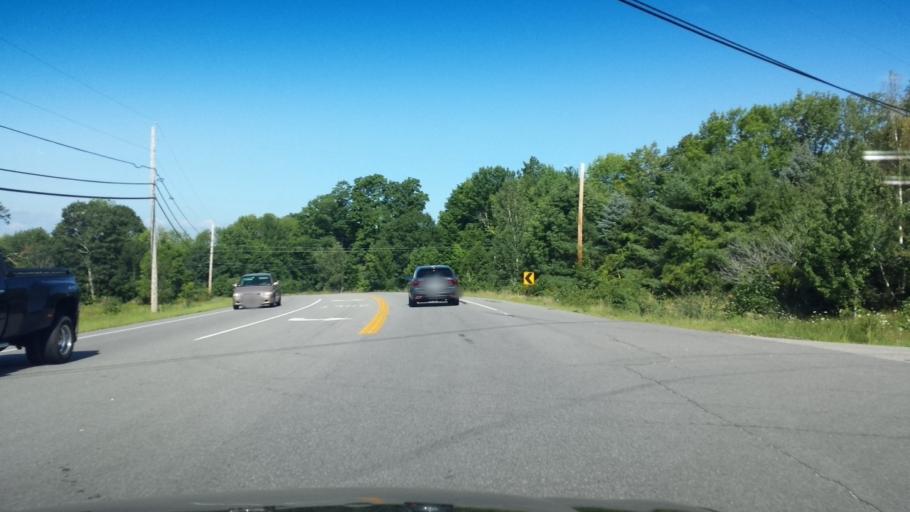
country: US
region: Maine
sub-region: York County
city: Lebanon
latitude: 43.4277
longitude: -70.8338
